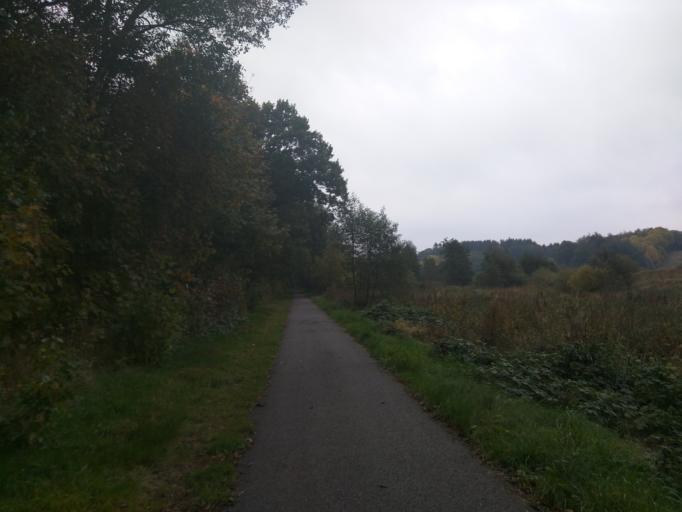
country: DK
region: Central Jutland
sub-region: Silkeborg Kommune
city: Silkeborg
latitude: 56.2346
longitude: 9.5240
